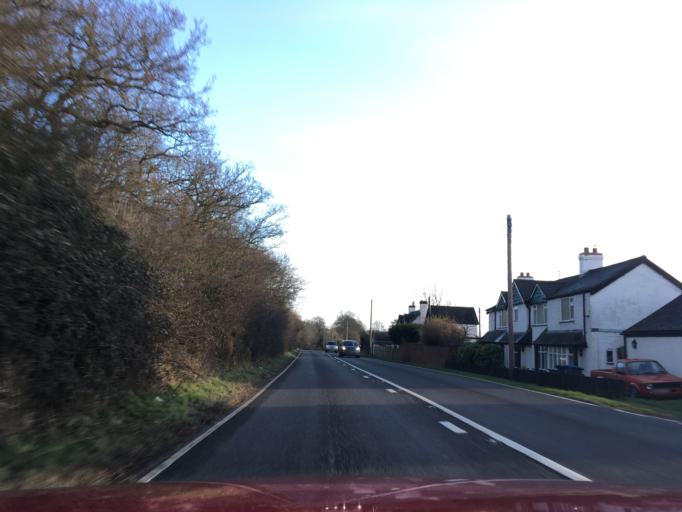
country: GB
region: England
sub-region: Warwickshire
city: Henley in Arden
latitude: 52.2536
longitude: -1.7601
